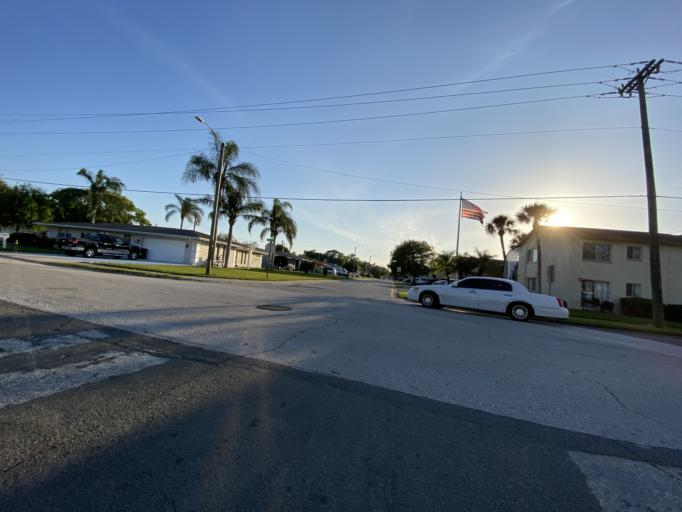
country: US
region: Florida
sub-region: Volusia County
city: South Daytona
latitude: 29.1804
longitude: -81.0131
